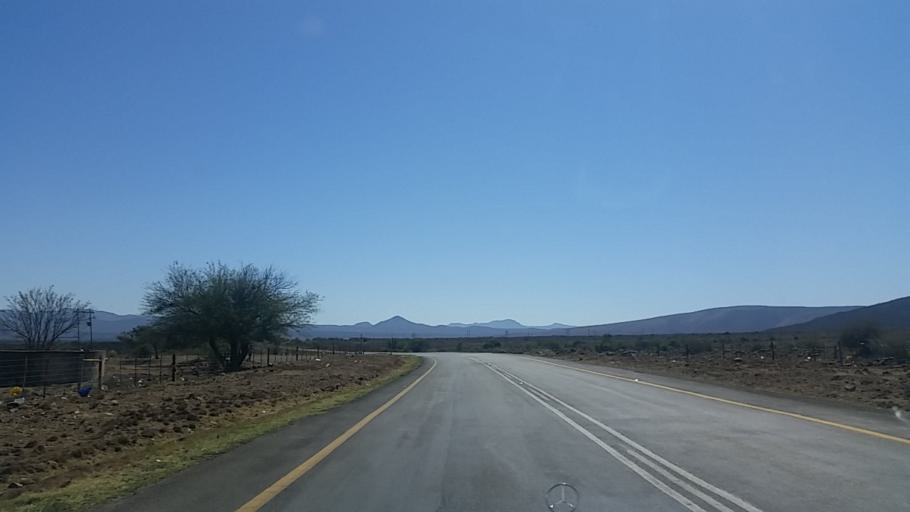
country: ZA
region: Eastern Cape
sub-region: Cacadu District Municipality
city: Graaff-Reinet
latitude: -32.2318
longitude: 24.5360
